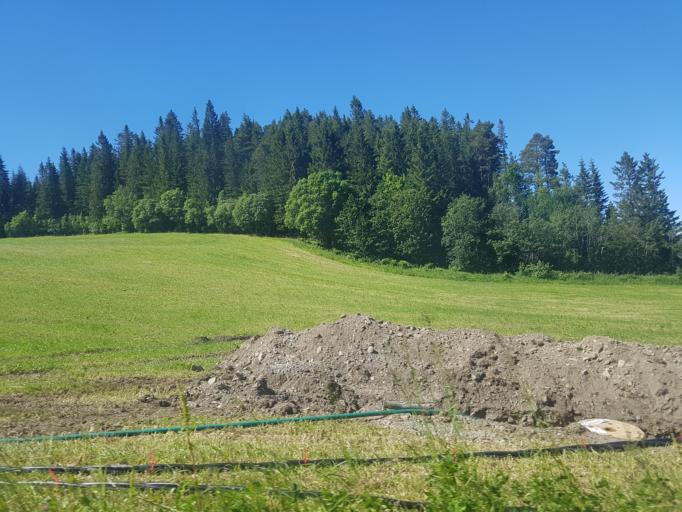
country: NO
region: Sor-Trondelag
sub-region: Skaun
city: Borsa
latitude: 63.4392
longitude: 10.1983
